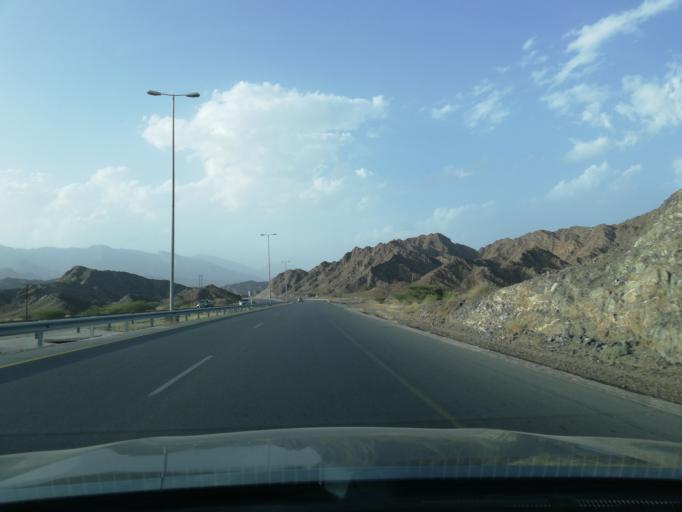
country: OM
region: Muhafazat ad Dakhiliyah
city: Izki
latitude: 22.9430
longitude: 57.7901
